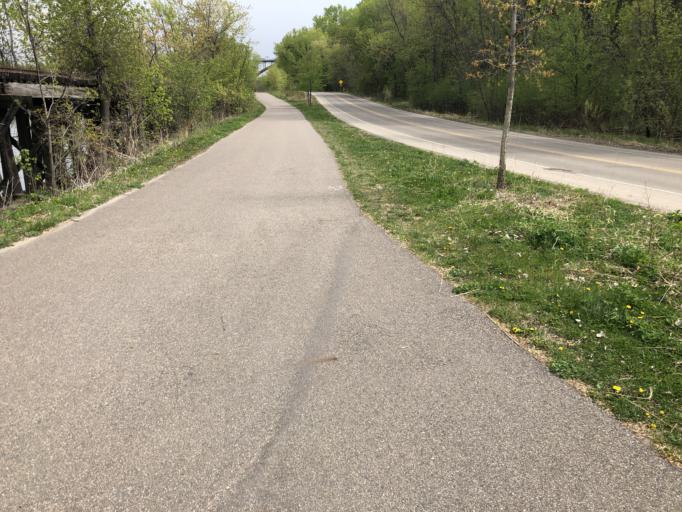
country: US
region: Minnesota
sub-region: Dakota County
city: West Saint Paul
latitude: 44.9257
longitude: -93.1104
